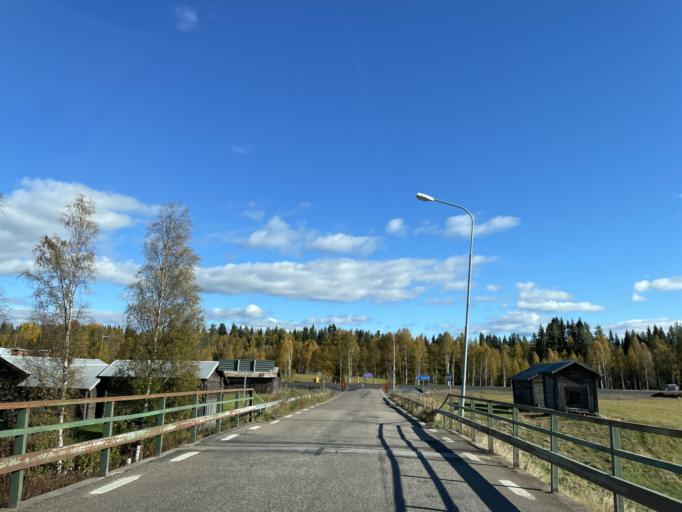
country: SE
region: Dalarna
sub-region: Malung-Saelens kommun
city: Malung
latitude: 60.8434
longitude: 13.4140
